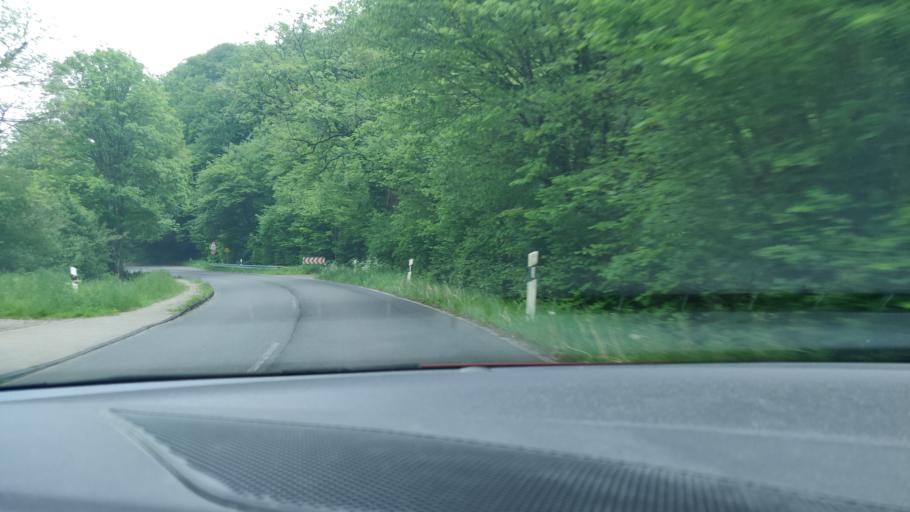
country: DE
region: North Rhine-Westphalia
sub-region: Regierungsbezirk Dusseldorf
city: Velbert
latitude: 51.3389
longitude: 7.0841
